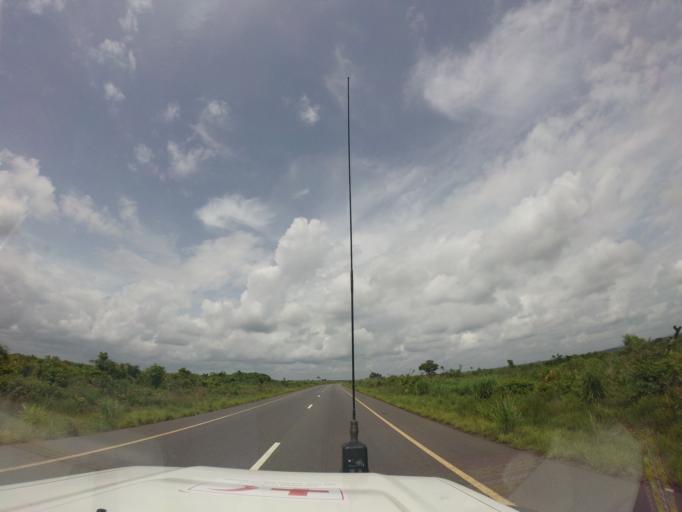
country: SL
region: Northern Province
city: Port Loko
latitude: 8.7457
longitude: -12.7428
